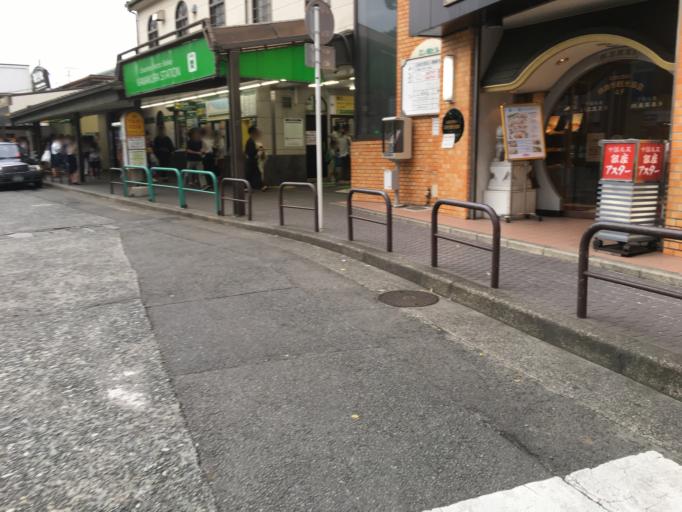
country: JP
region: Kanagawa
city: Kamakura
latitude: 35.3187
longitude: 139.5499
